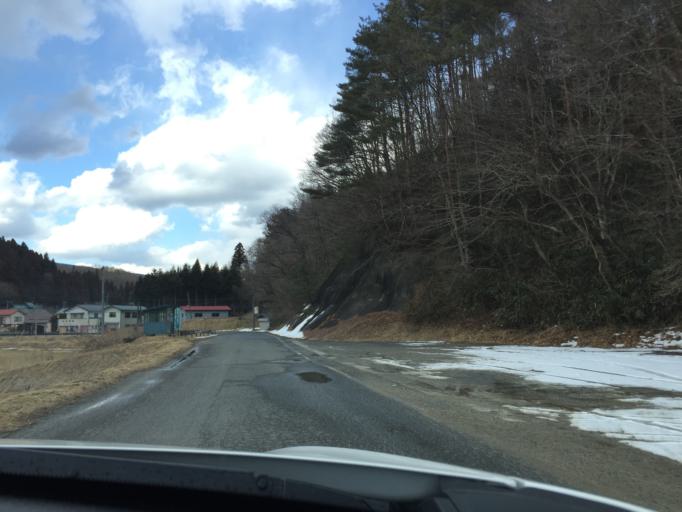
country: JP
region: Fukushima
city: Iwaki
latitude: 37.2427
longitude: 140.7272
